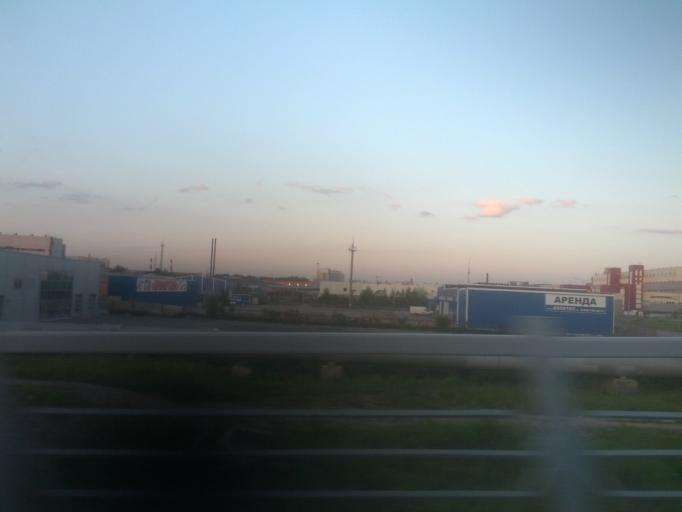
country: RU
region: St.-Petersburg
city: Staraya Derevnya
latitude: 59.9926
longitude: 30.2327
